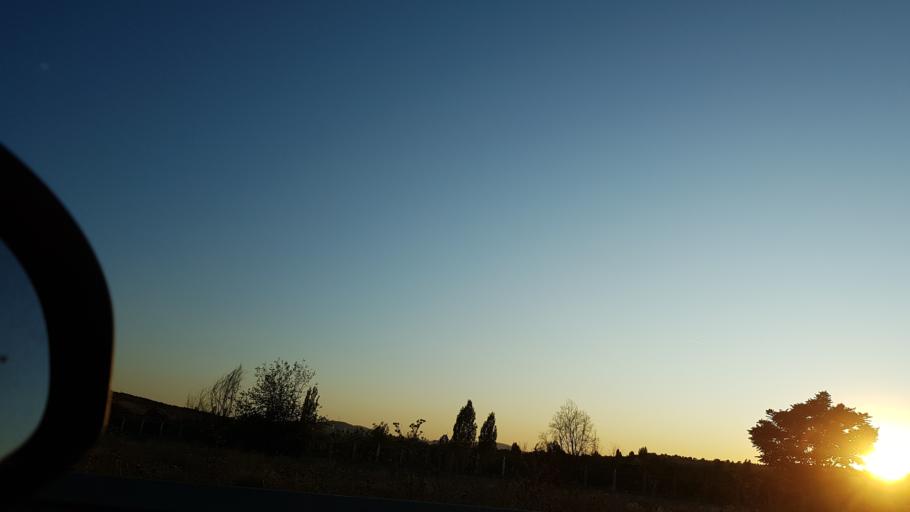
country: TR
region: Ankara
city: Batikent
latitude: 39.9244
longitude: 32.7054
